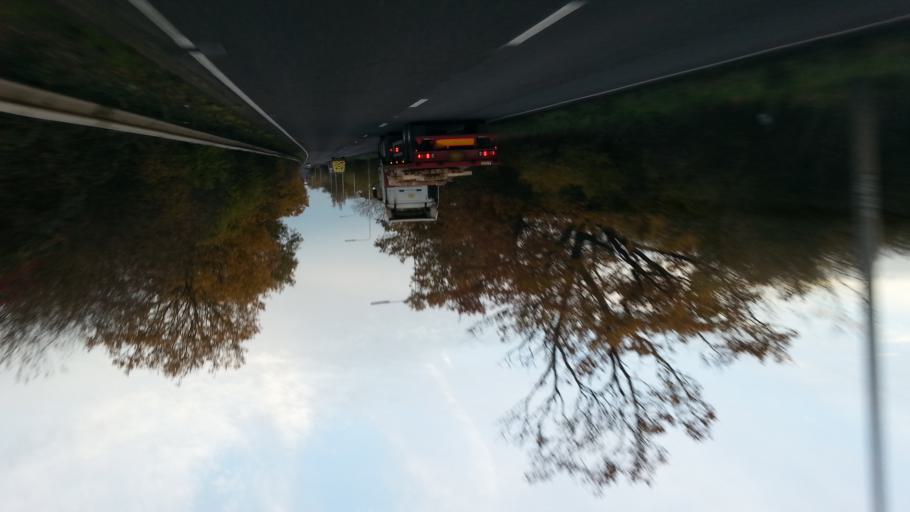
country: GB
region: England
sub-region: Central Bedfordshire
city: Astwick
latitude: 52.0376
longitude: -0.2201
